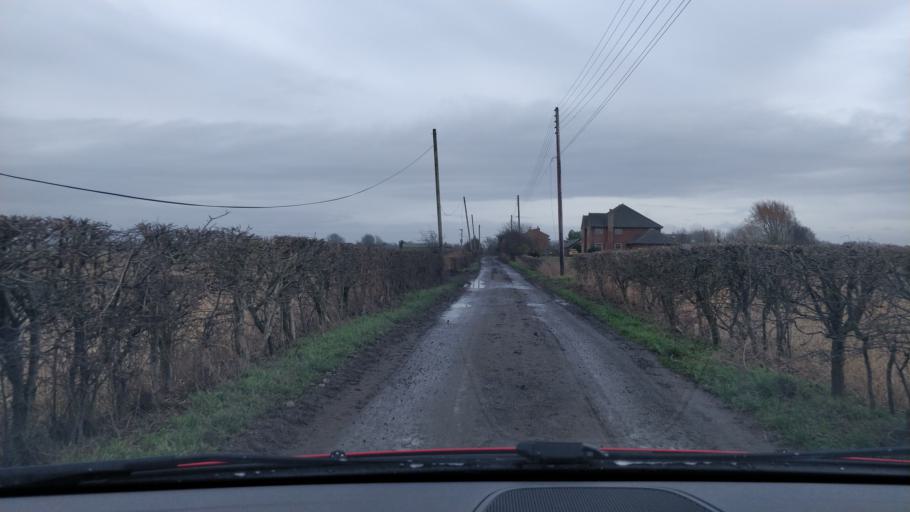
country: GB
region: England
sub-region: Lancashire
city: Banks
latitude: 53.6861
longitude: -2.9327
